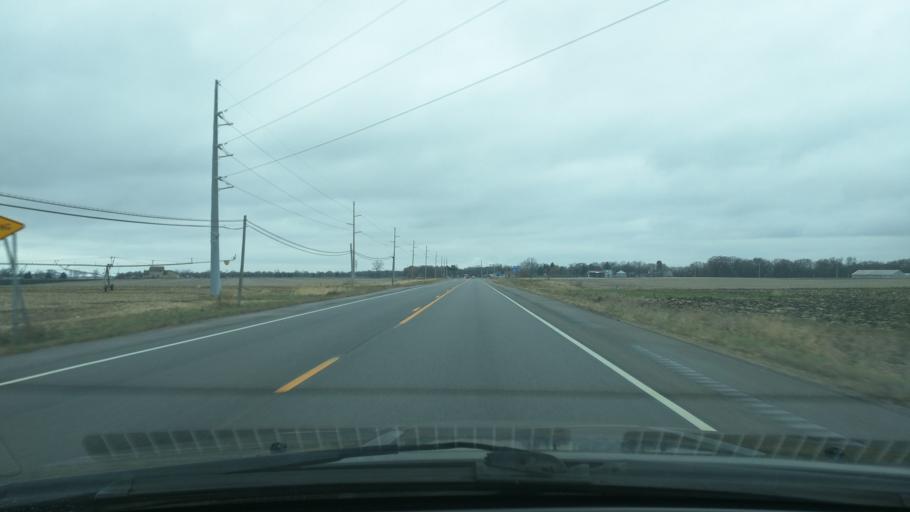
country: US
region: Minnesota
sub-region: Washington County
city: Cottage Grove
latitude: 44.7393
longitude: -92.9422
